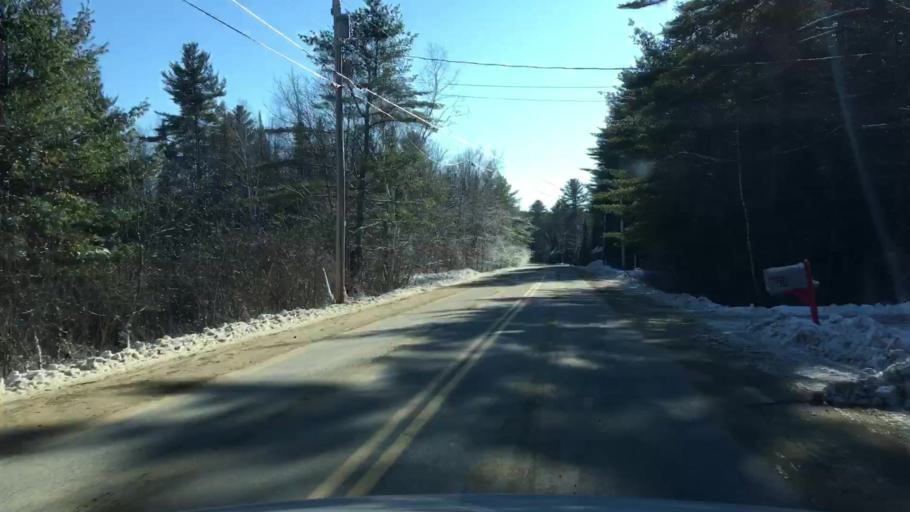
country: US
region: Maine
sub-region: Kennebec County
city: Readfield
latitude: 44.3577
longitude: -69.9911
